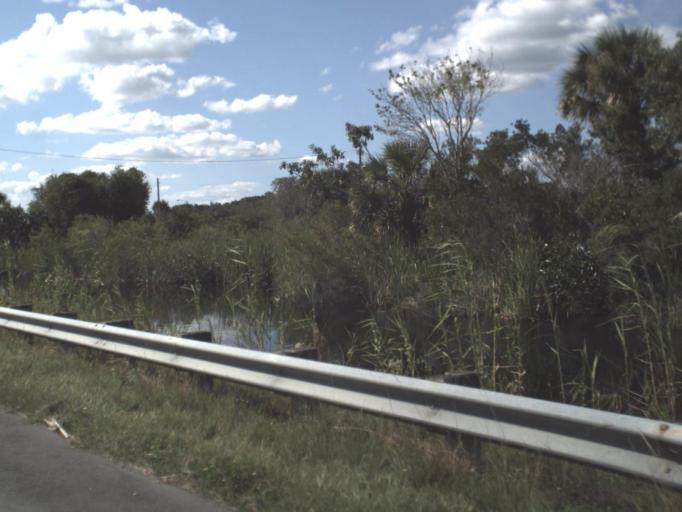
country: US
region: Florida
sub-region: Collier County
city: Marco
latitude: 25.9014
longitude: -81.3339
